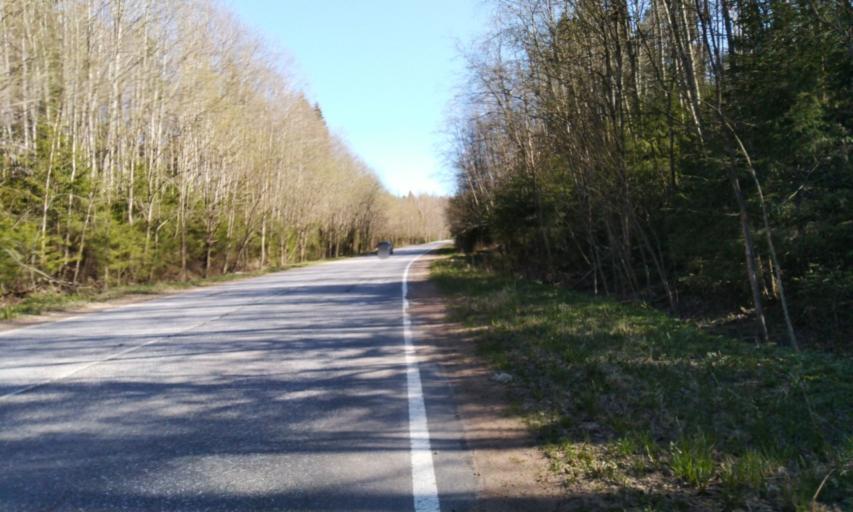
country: RU
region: Leningrad
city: Garbolovo
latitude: 60.3694
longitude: 30.4409
